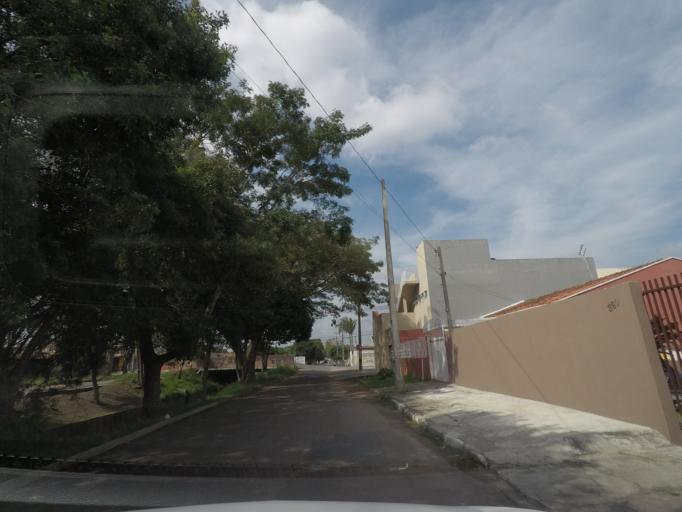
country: BR
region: Parana
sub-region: Pinhais
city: Pinhais
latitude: -25.4734
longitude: -49.1951
